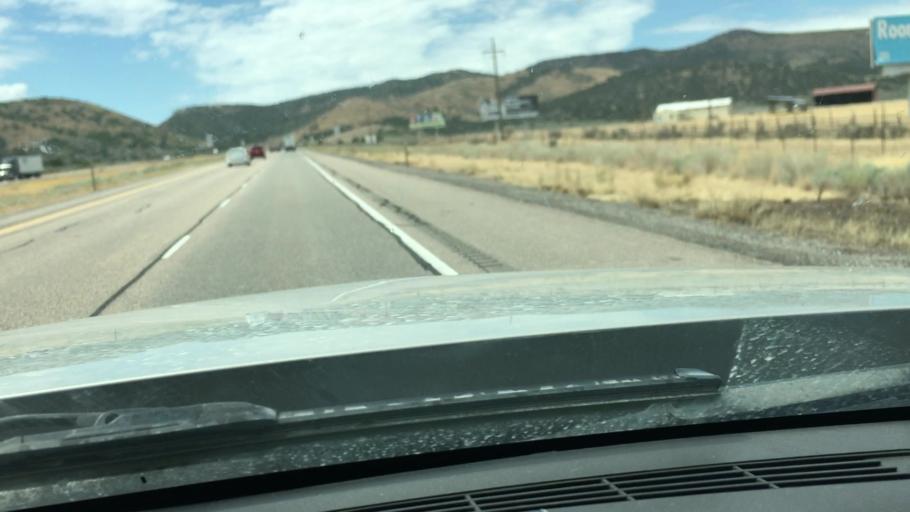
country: US
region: Utah
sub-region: Millard County
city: Fillmore
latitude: 39.2328
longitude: -112.1405
